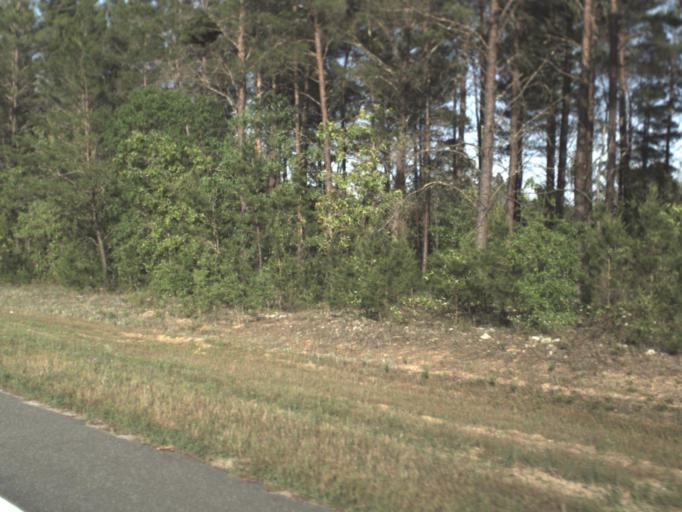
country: US
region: Florida
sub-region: Gadsden County
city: Gretna
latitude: 30.4593
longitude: -84.7428
